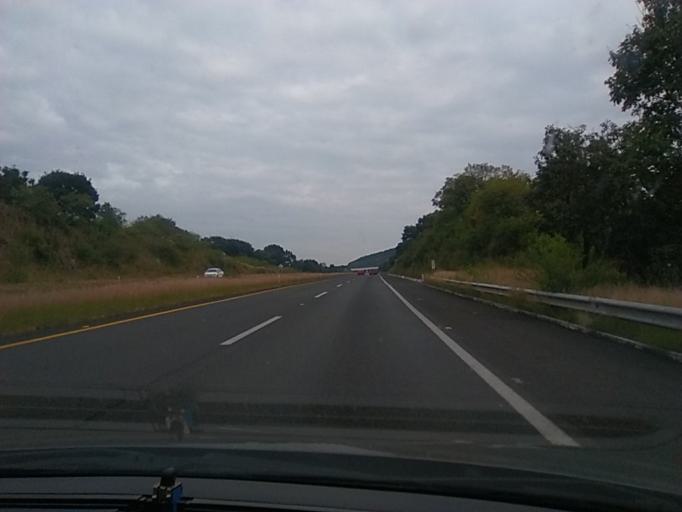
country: MX
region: Michoacan
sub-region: Puruandiro
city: San Lorenzo
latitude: 19.9654
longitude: -101.6993
